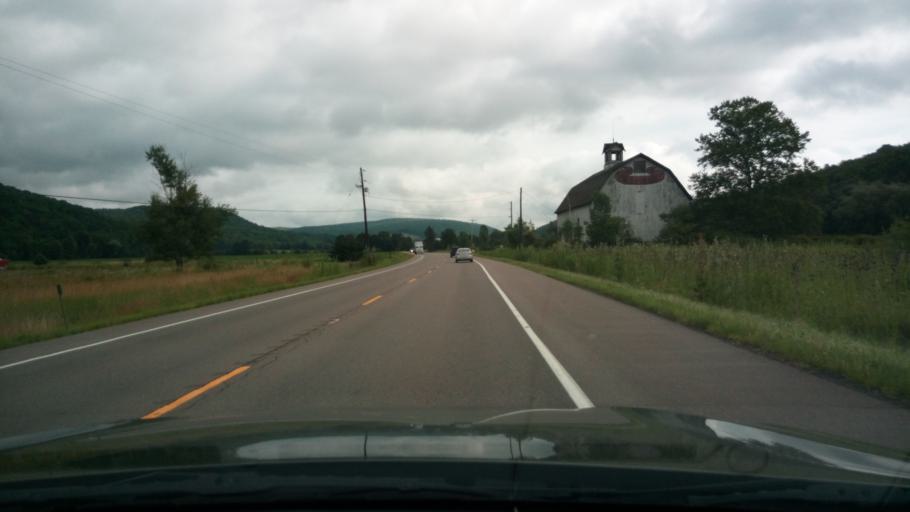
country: US
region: New York
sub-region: Chemung County
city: Horseheads North
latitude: 42.3062
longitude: -76.6752
